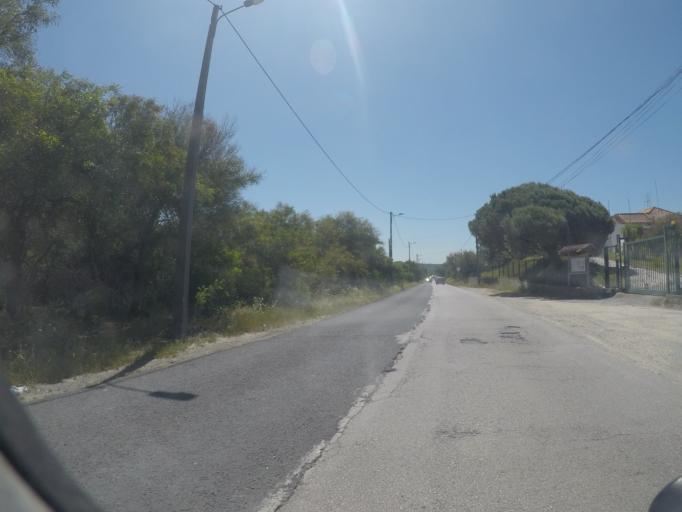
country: PT
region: Setubal
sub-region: Almada
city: Charneca
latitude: 38.6176
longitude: -9.2123
